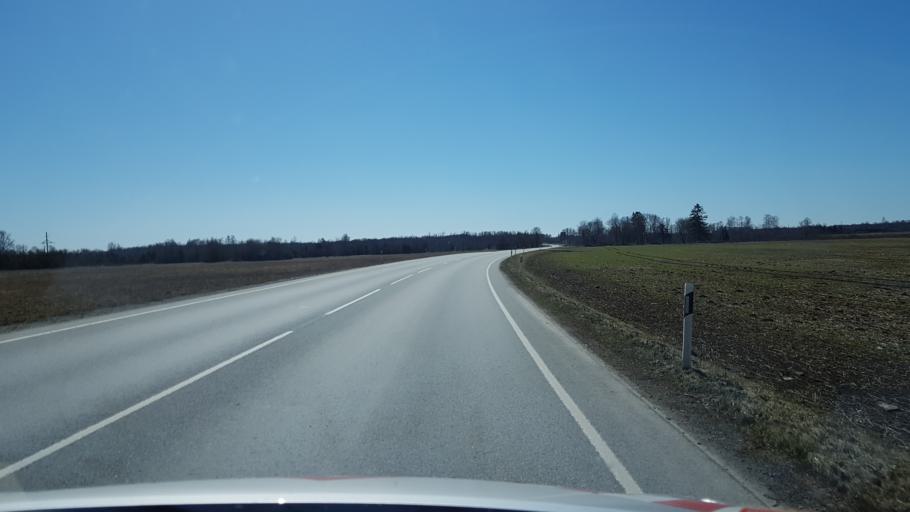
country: EE
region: Laeaene-Virumaa
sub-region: Viru-Nigula vald
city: Kunda
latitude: 59.4681
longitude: 26.4785
